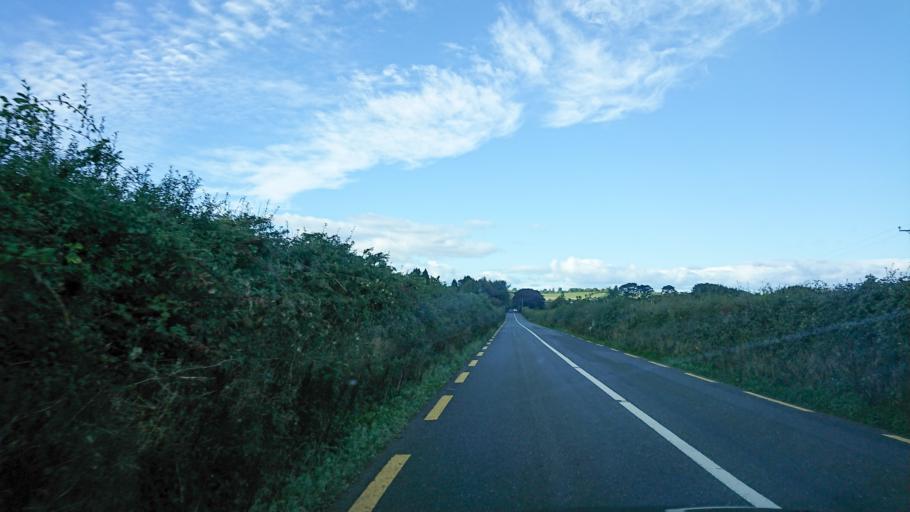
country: IE
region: Munster
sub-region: Waterford
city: Dungarvan
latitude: 52.1405
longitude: -7.6933
